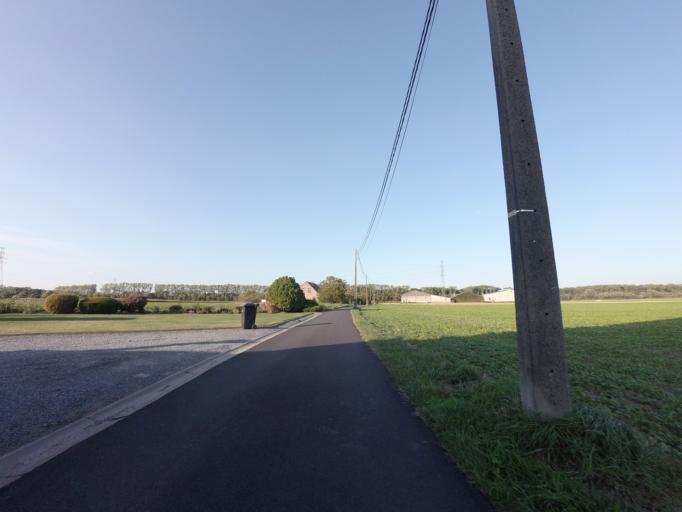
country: BE
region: Flanders
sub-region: Provincie Vlaams-Brabant
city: Haacht
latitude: 50.9472
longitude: 4.6157
